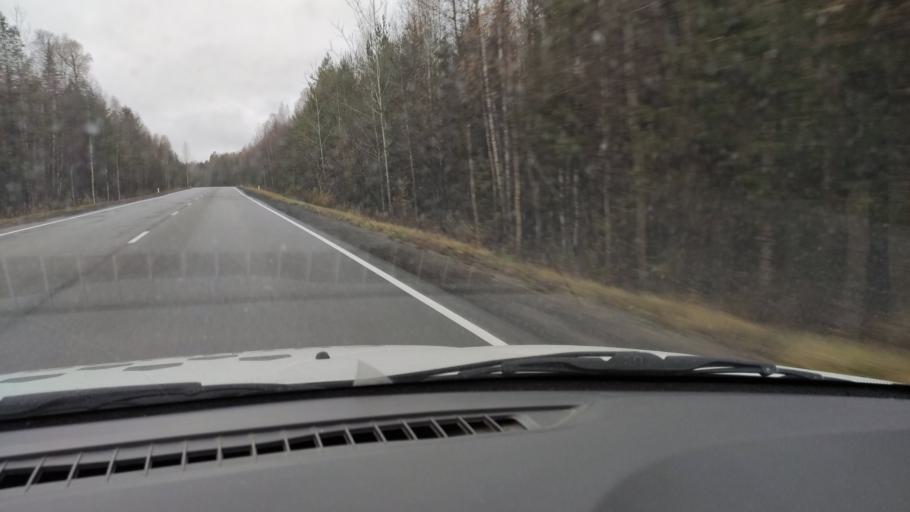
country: RU
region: Kirov
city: Chernaya Kholunitsa
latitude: 58.8670
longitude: 51.5686
